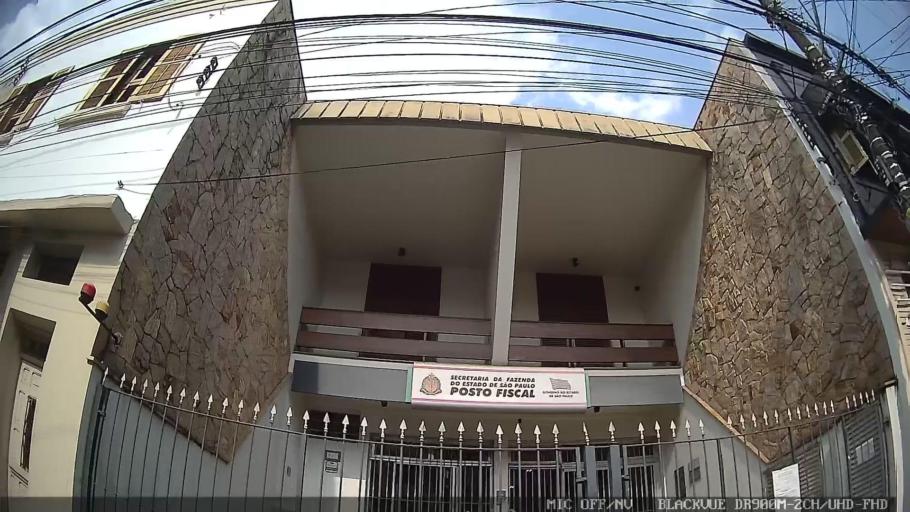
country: BR
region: Sao Paulo
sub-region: Braganca Paulista
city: Braganca Paulista
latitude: -22.9541
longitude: -46.5415
